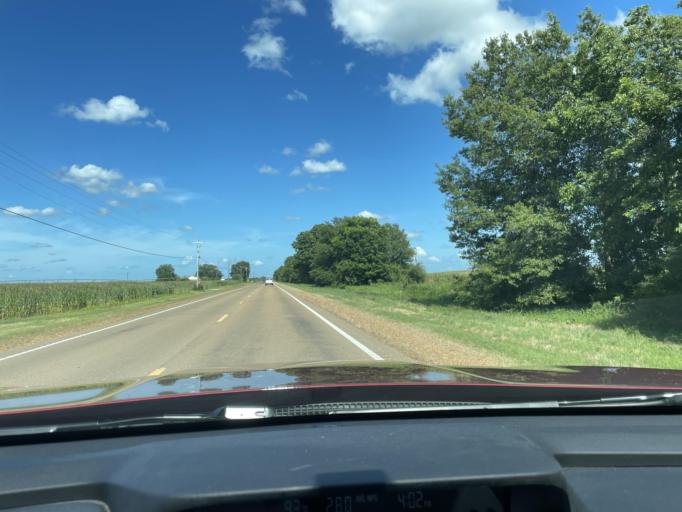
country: US
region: Mississippi
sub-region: Humphreys County
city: Belzoni
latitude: 33.1837
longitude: -90.5289
